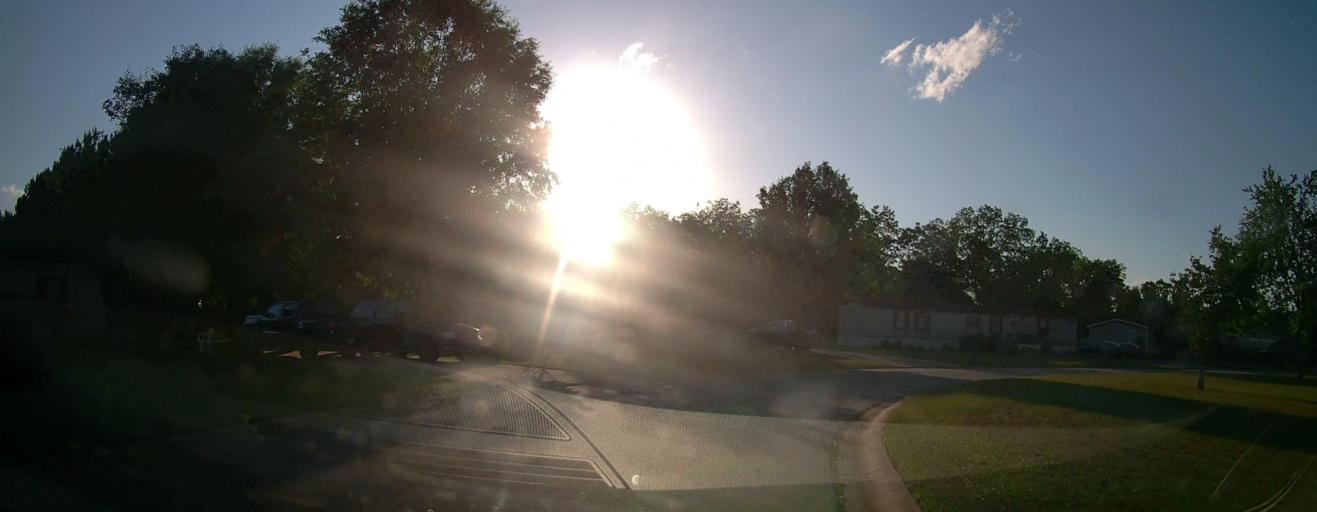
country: US
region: Georgia
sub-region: Peach County
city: Byron
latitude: 32.6362
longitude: -83.7272
